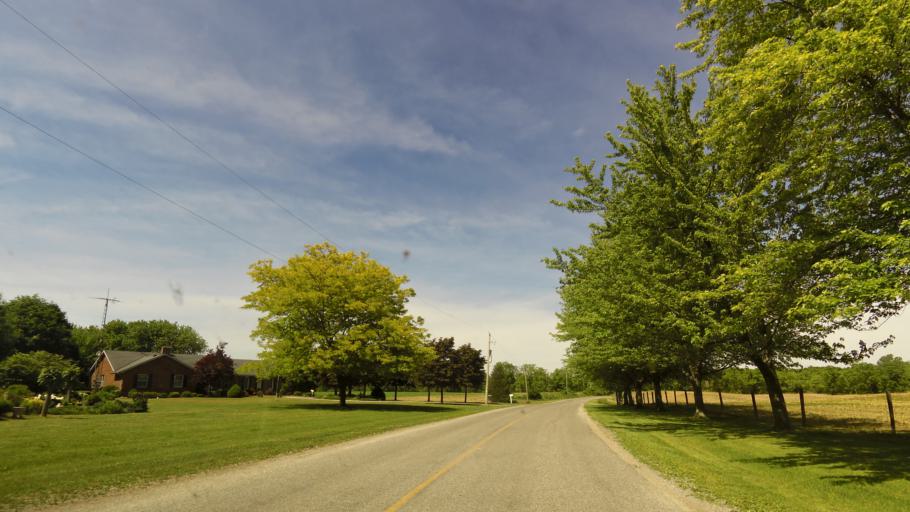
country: CA
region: Ontario
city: Norfolk County
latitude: 42.7292
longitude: -80.2913
